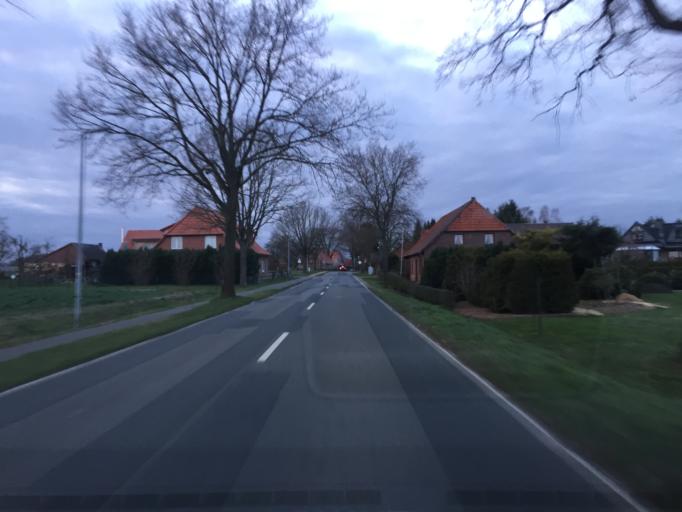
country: DE
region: Lower Saxony
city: Steimbke
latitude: 52.5906
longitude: 9.4023
